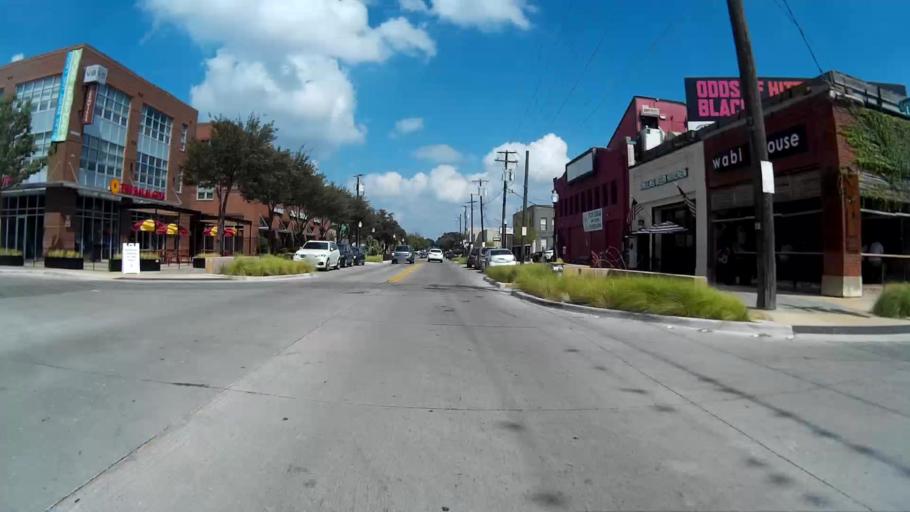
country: US
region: Texas
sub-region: Dallas County
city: Highland Park
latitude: 32.8122
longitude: -96.7702
